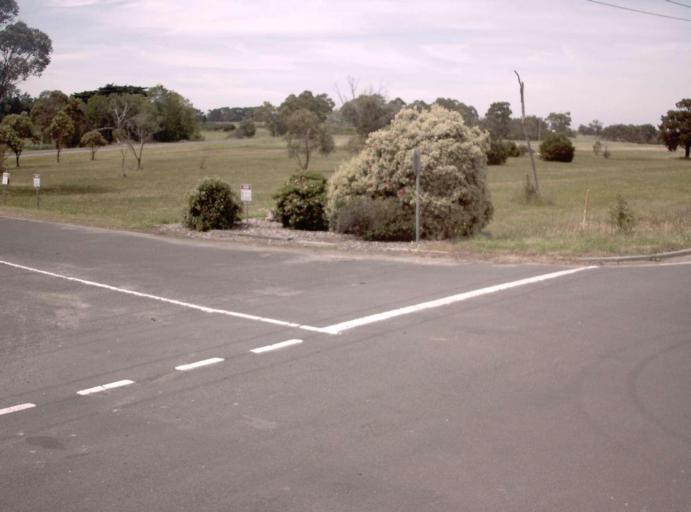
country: AU
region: Victoria
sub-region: Mornington Peninsula
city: Hastings
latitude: -38.2763
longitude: 145.1894
